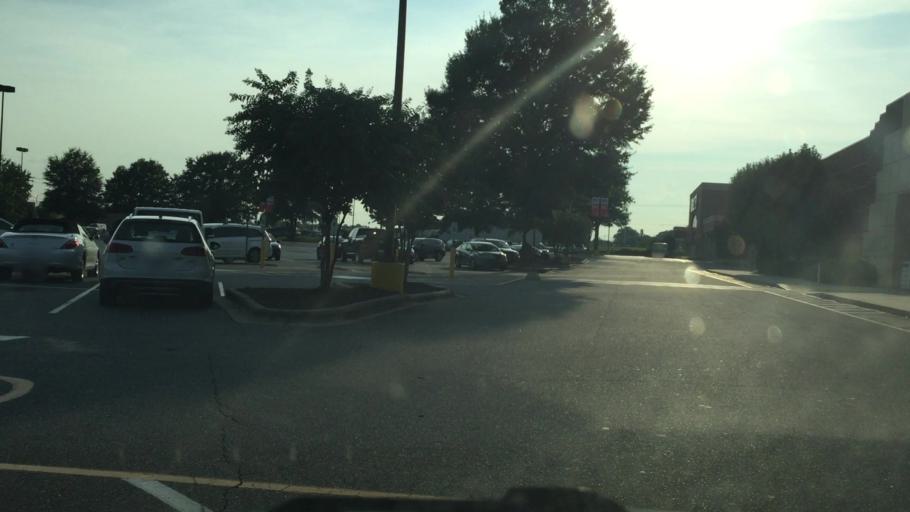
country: US
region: North Carolina
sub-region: Iredell County
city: Mooresville
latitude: 35.5953
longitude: -80.8549
